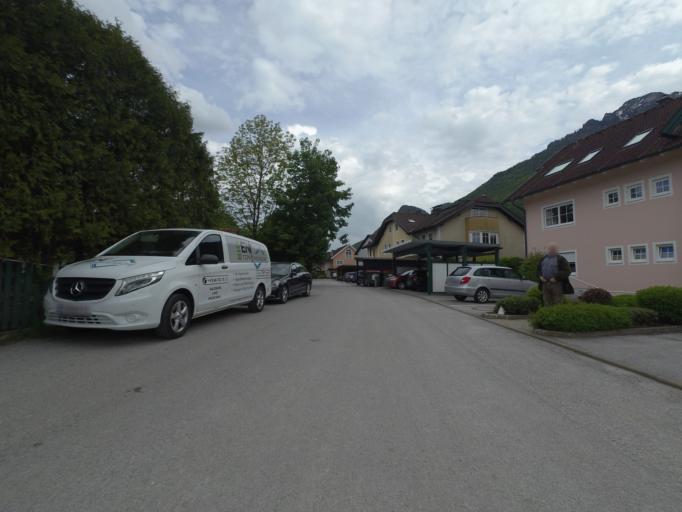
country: AT
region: Salzburg
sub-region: Politischer Bezirk Salzburg-Umgebung
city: Grodig
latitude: 47.7490
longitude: 12.9975
